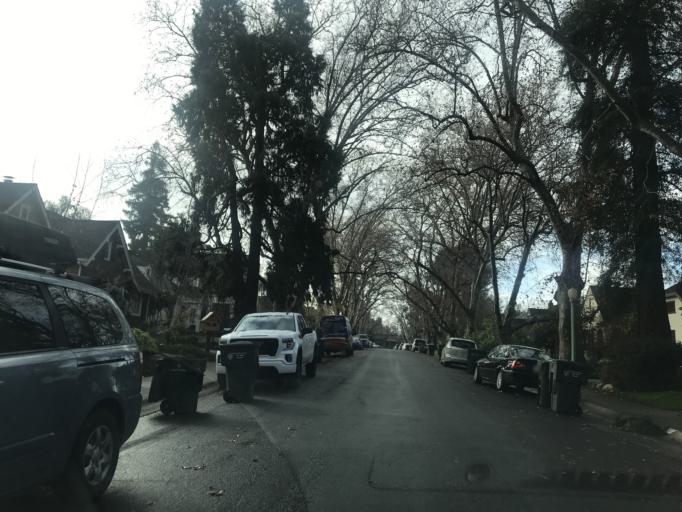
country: US
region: California
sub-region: Sacramento County
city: Sacramento
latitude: 38.5759
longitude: -121.4587
